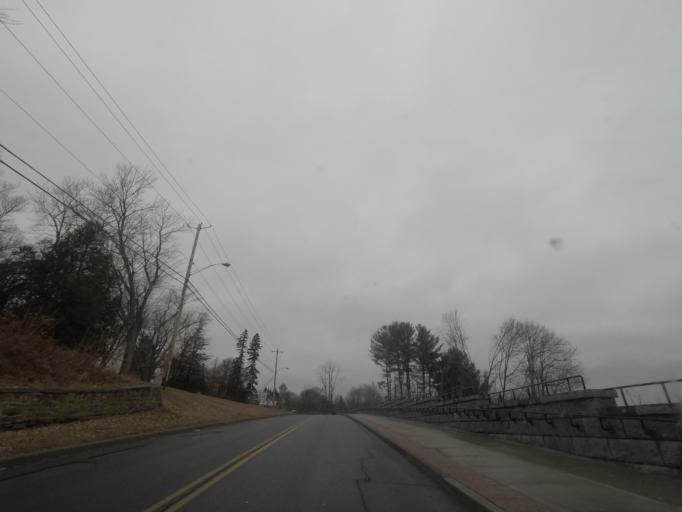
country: US
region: New York
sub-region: Saratoga County
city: Mechanicville
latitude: 42.9000
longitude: -73.6934
